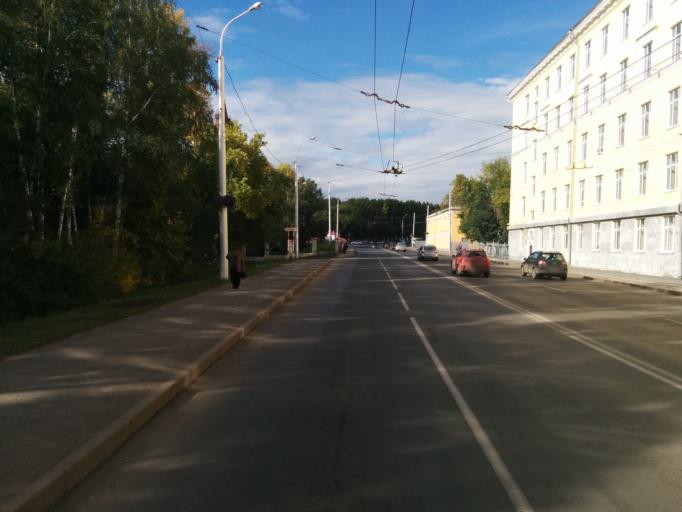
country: RU
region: Bashkortostan
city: Ufa
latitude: 54.8181
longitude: 56.0574
